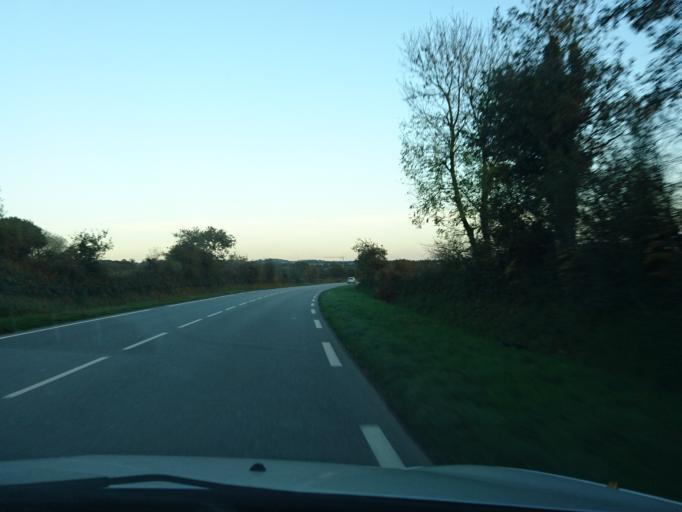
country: FR
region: Brittany
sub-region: Departement du Finistere
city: Saint-Renan
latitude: 48.4313
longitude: -4.6059
